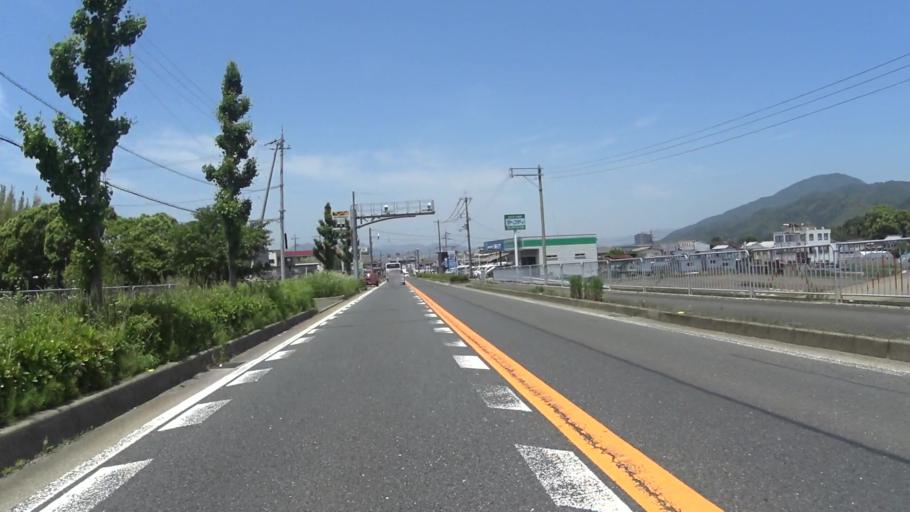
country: JP
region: Kyoto
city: Kameoka
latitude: 34.9991
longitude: 135.6110
